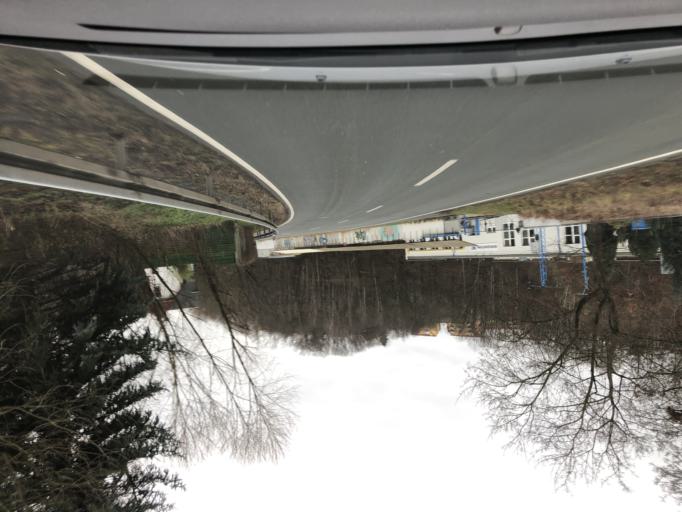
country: DE
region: Saxony
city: Rosswein
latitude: 51.0704
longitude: 13.1733
